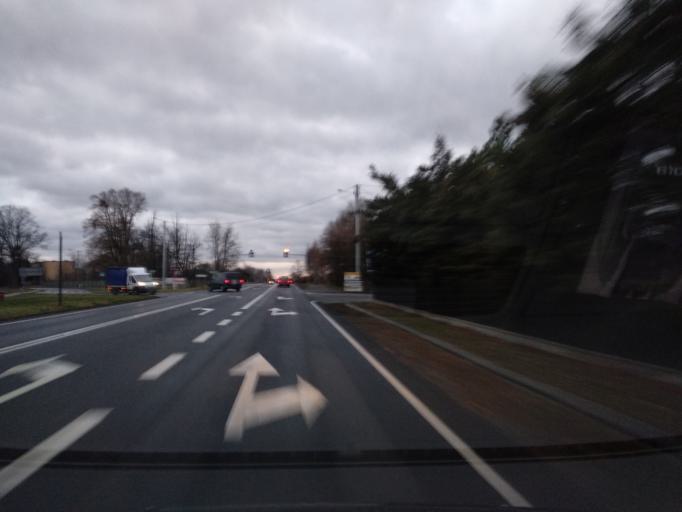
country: PL
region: Greater Poland Voivodeship
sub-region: Powiat koninski
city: Rychwal
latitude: 52.0786
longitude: 18.1602
